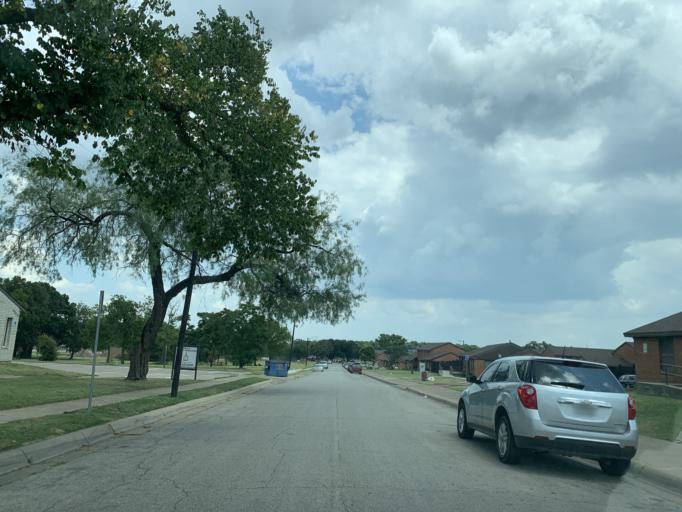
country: US
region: Texas
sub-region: Tarrant County
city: Forest Hill
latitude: 32.7302
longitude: -97.2471
